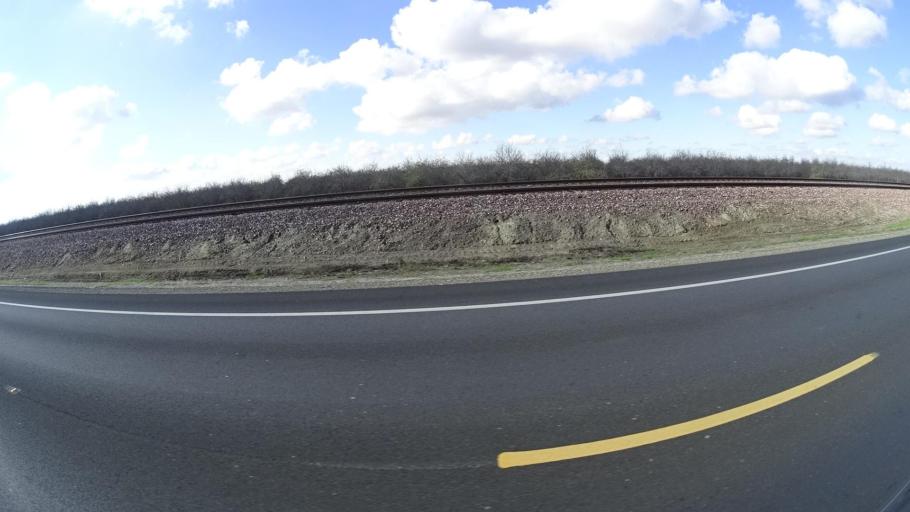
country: US
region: California
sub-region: Kern County
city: Wasco
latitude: 35.6862
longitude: -119.3306
